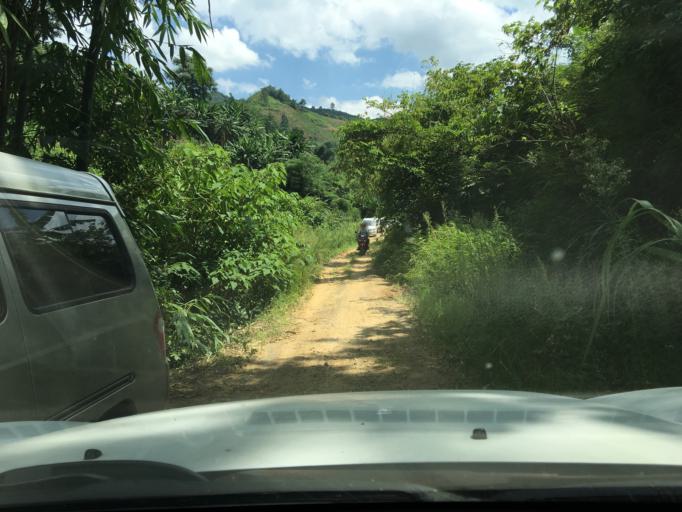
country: CN
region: Guangxi Zhuangzu Zizhiqu
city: Tongle
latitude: 24.9716
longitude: 105.9855
